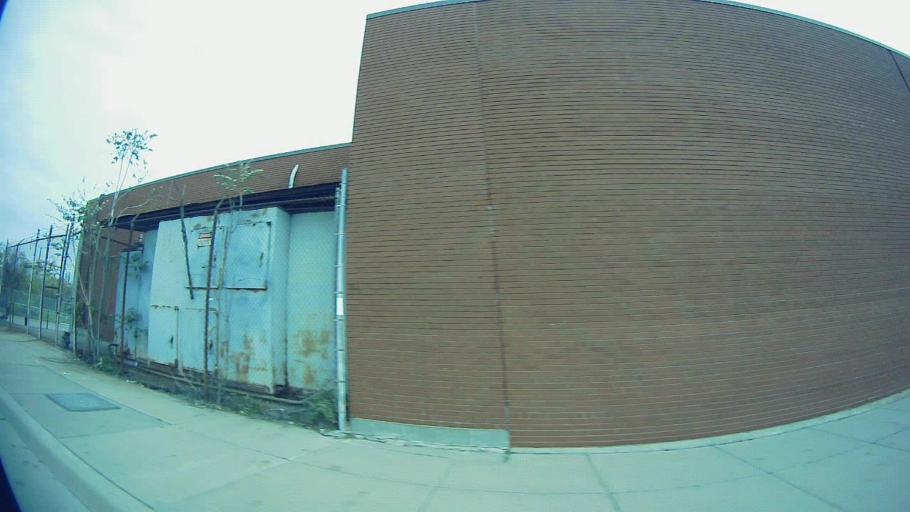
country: US
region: Michigan
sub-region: Wayne County
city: Hamtramck
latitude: 42.3638
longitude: -83.0520
